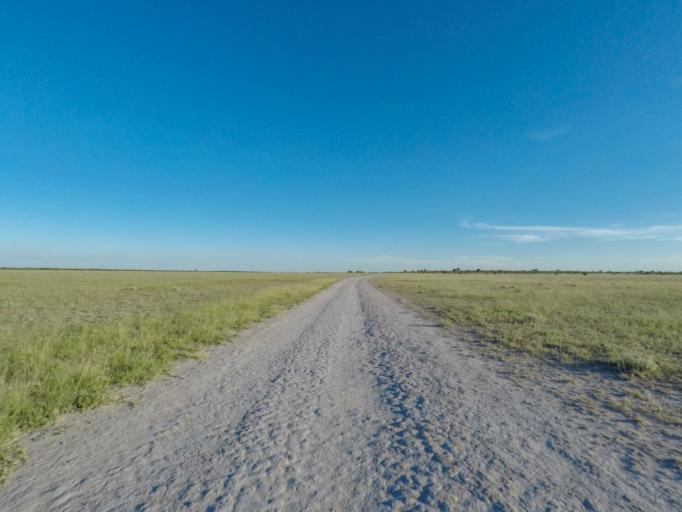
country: BW
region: Central
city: Rakops
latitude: -21.3973
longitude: 23.7945
